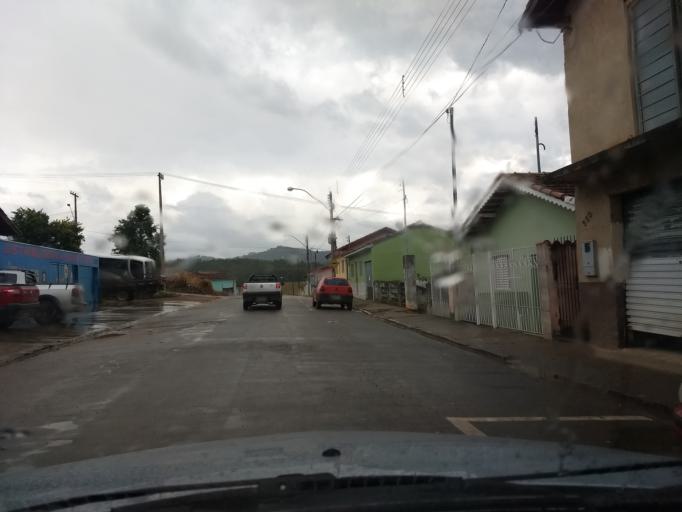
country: BR
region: Minas Gerais
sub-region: Extrema
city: Extrema
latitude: -22.7439
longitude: -46.3735
